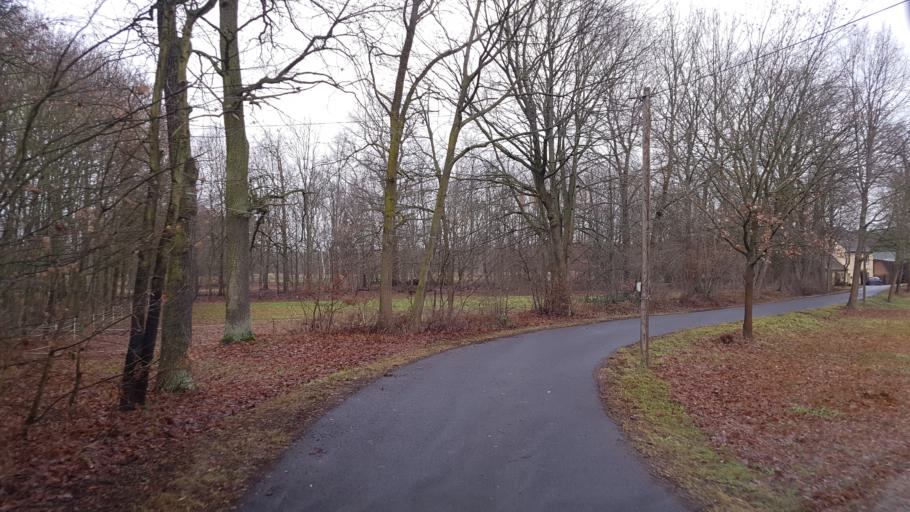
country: DE
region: Brandenburg
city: Altdobern
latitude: 51.6921
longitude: 14.0391
